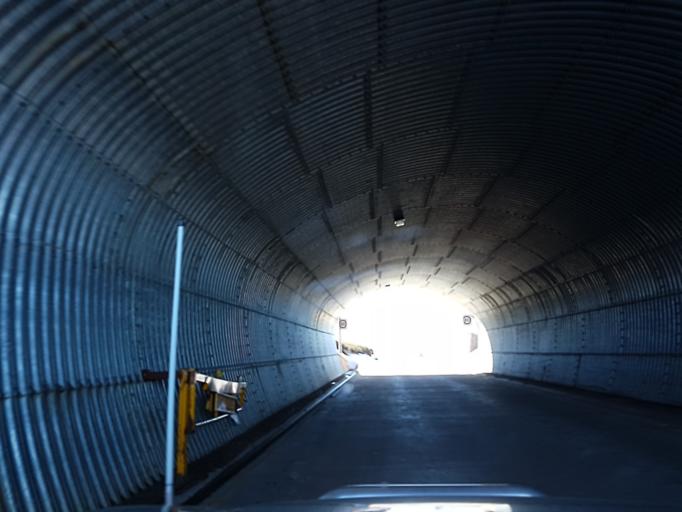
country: AU
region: Victoria
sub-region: Alpine
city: Mount Beauty
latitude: -36.9795
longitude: 147.1420
